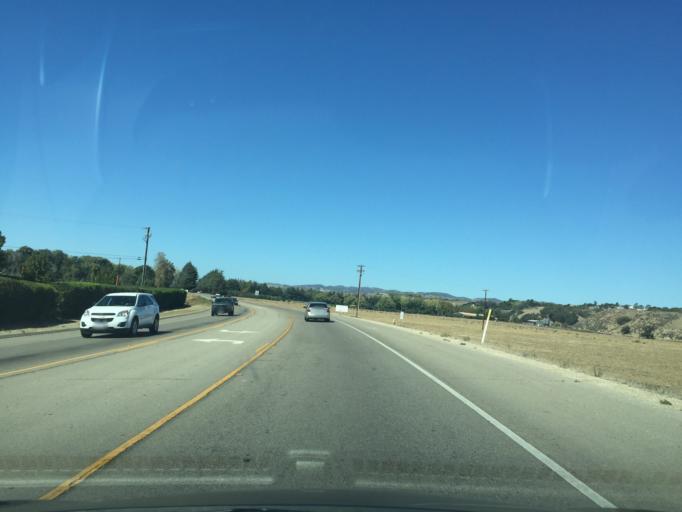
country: US
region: California
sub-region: Santa Barbara County
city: Solvang
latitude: 34.5970
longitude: -120.1555
